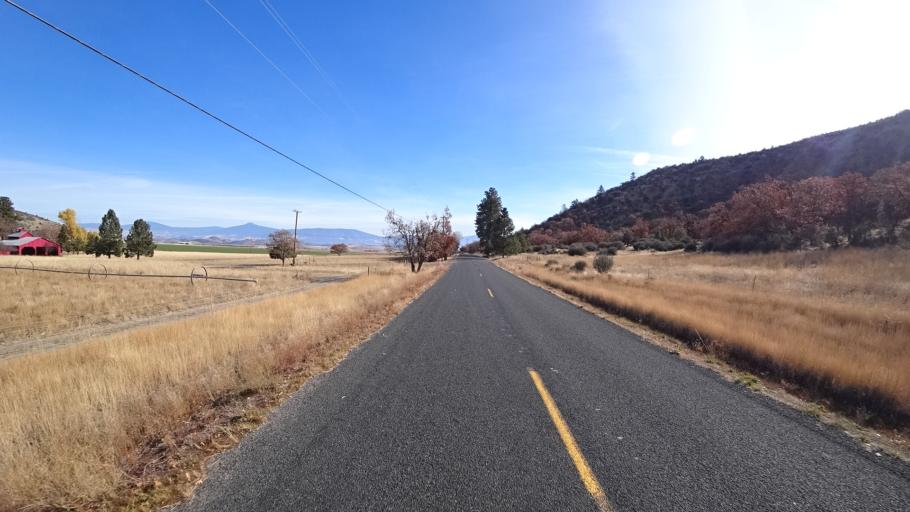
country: US
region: California
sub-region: Siskiyou County
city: Montague
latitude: 41.5389
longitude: -122.5761
